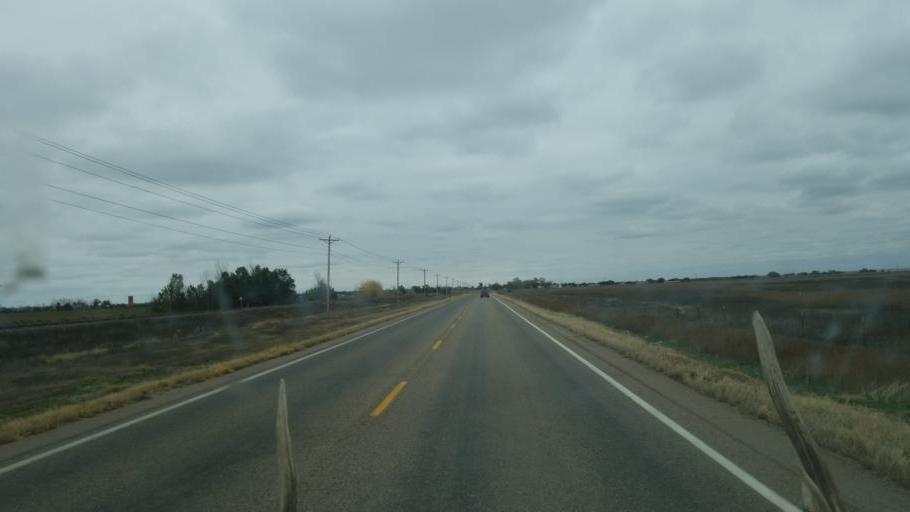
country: US
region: Colorado
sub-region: Crowley County
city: Ordway
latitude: 38.2081
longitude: -103.7936
